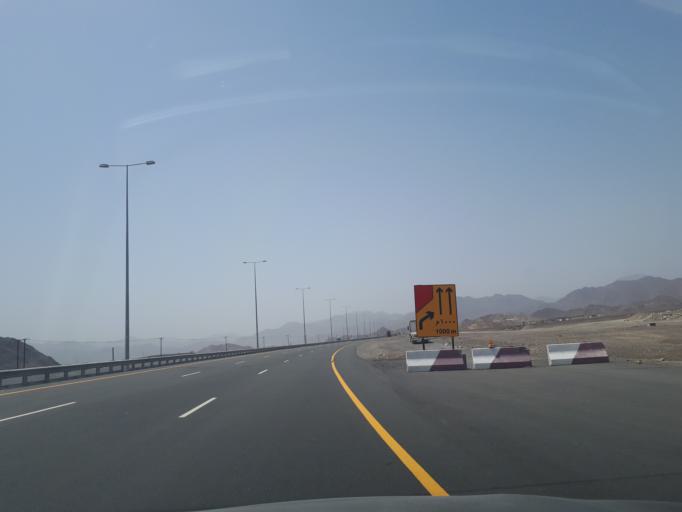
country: OM
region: Muhafazat ad Dakhiliyah
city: Sufalat Sama'il
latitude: 23.3059
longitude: 58.1106
